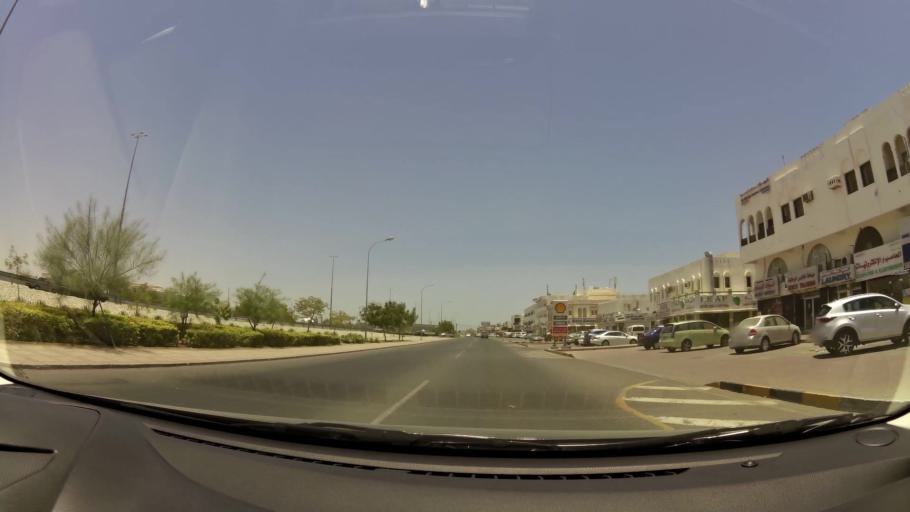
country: OM
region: Muhafazat Masqat
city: As Sib al Jadidah
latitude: 23.6312
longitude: 58.2329
